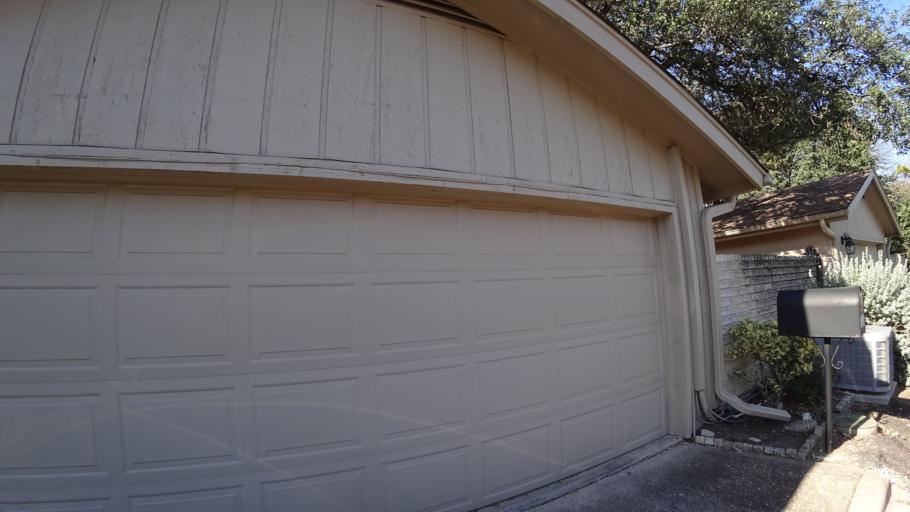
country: US
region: Texas
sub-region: Williamson County
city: Jollyville
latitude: 30.3718
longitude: -97.7478
